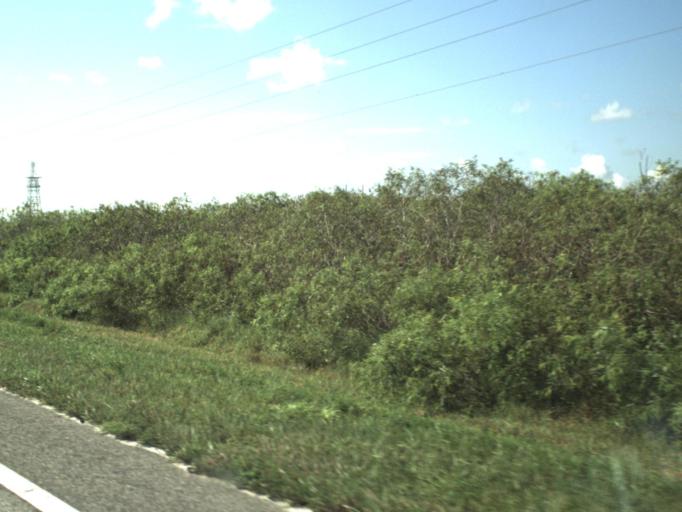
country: US
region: Florida
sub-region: Broward County
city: Weston
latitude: 26.3081
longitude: -80.5174
